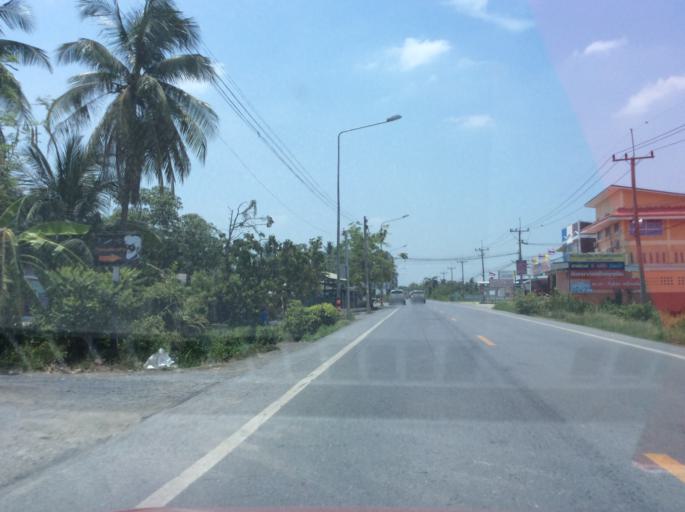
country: TH
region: Pathum Thani
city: Ban Lam Luk Ka
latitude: 13.9893
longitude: 100.7778
